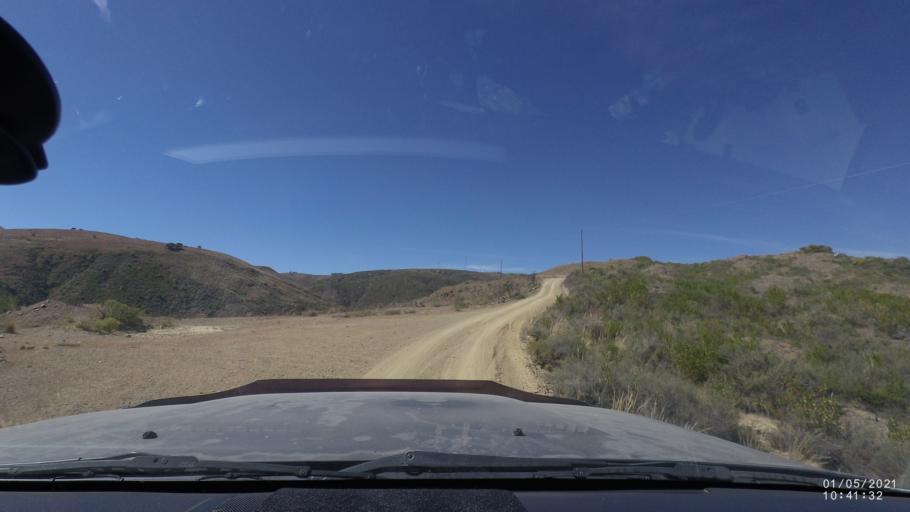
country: BO
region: Cochabamba
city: Capinota
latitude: -17.6086
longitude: -66.1770
